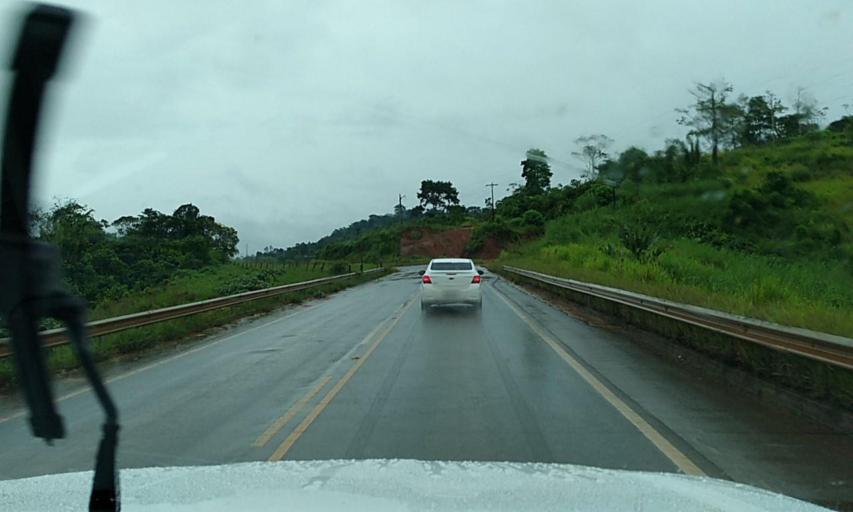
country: BR
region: Para
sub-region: Altamira
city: Altamira
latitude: -3.3137
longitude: -52.5563
